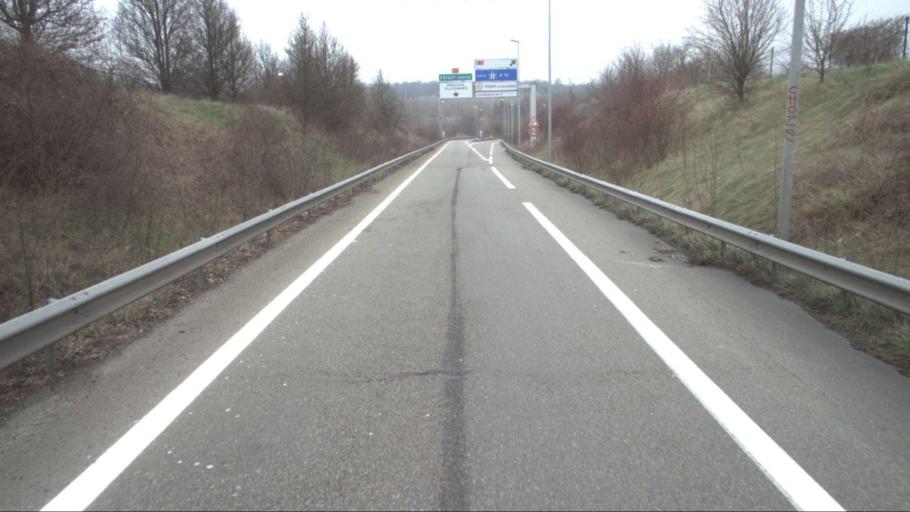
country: FR
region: Ile-de-France
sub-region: Departement des Yvelines
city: Orgeval
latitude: 48.9154
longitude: 2.0059
